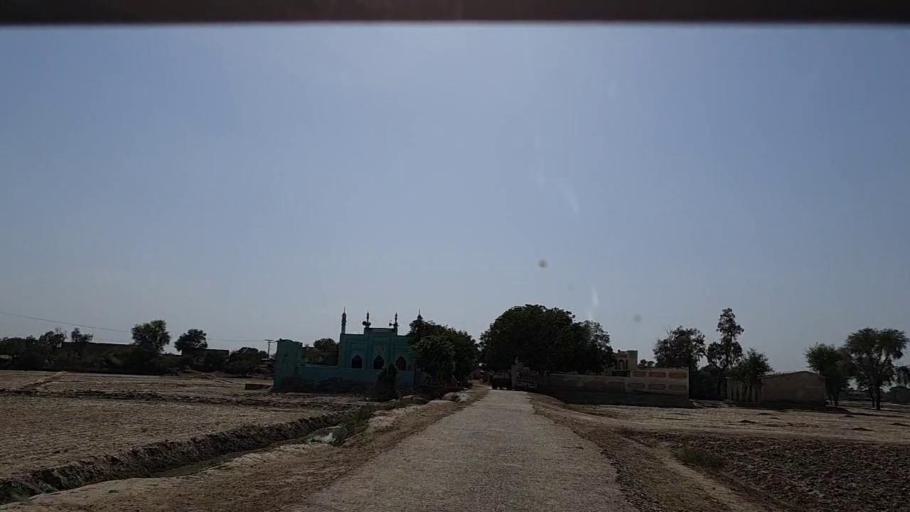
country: PK
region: Sindh
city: Phulji
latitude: 26.9510
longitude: 67.6819
